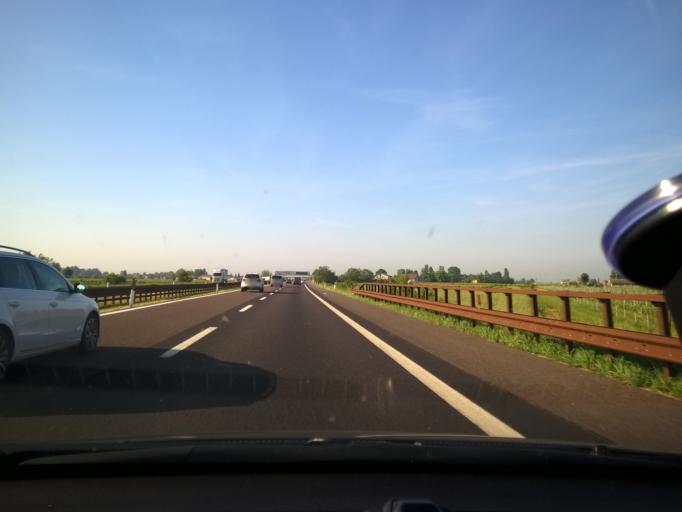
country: IT
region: Emilia-Romagna
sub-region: Provincia di Modena
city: Santa Croce Scuole
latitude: 44.7419
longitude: 10.8445
